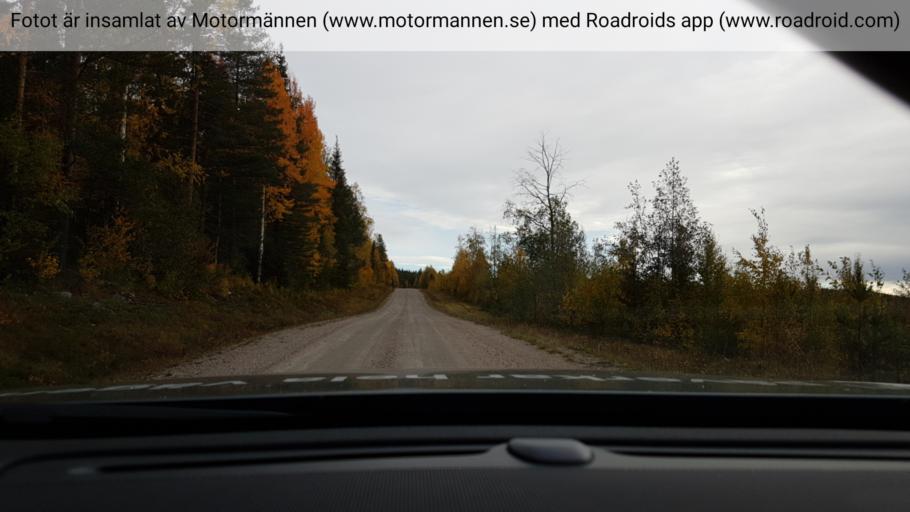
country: SE
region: Norrbotten
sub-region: Overkalix Kommun
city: OEverkalix
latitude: 66.2673
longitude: 23.0107
